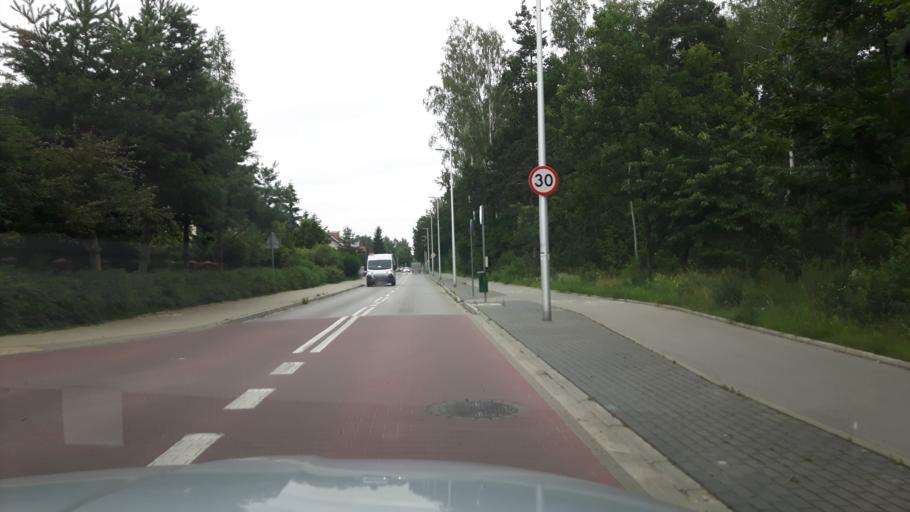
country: PL
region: Masovian Voivodeship
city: Zielonka
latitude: 52.2938
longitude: 21.1629
